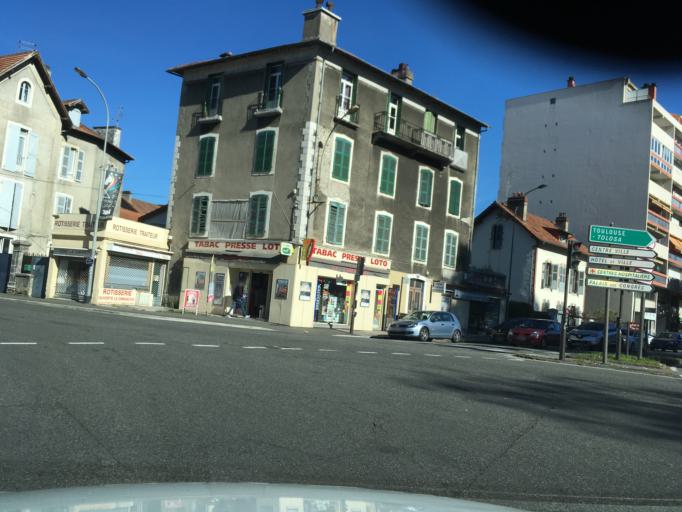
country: FR
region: Aquitaine
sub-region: Departement des Pyrenees-Atlantiques
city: Pau
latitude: 43.3057
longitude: -0.3763
